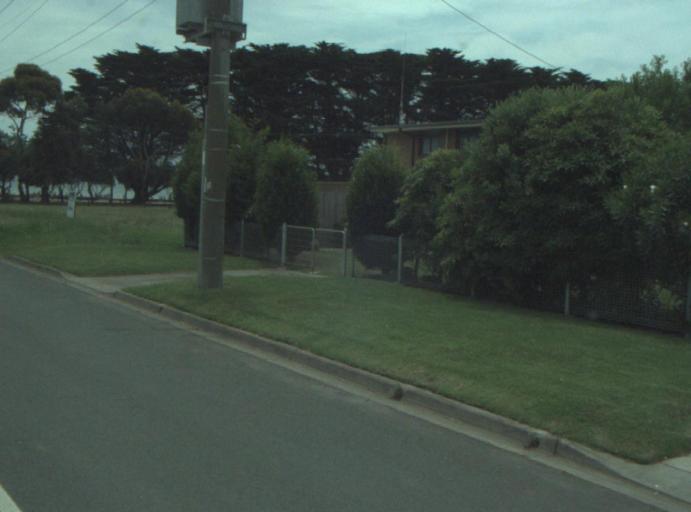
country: AU
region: Victoria
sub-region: Greater Geelong
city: Clifton Springs
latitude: -38.1132
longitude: 144.6464
